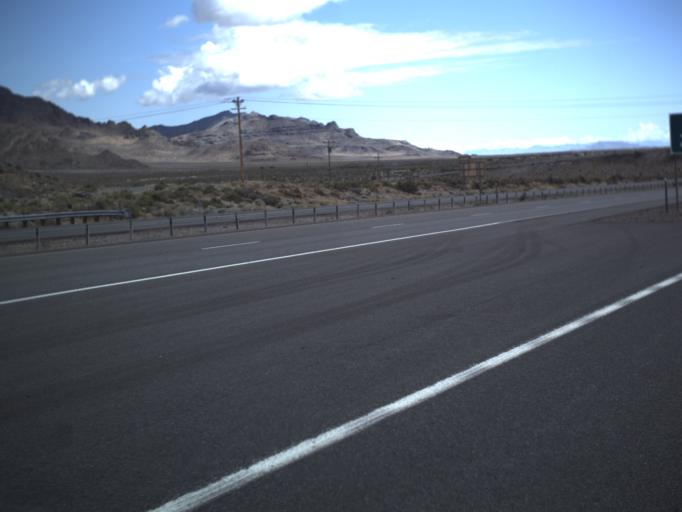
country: US
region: Utah
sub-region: Tooele County
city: Wendover
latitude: 40.7447
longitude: -114.0218
